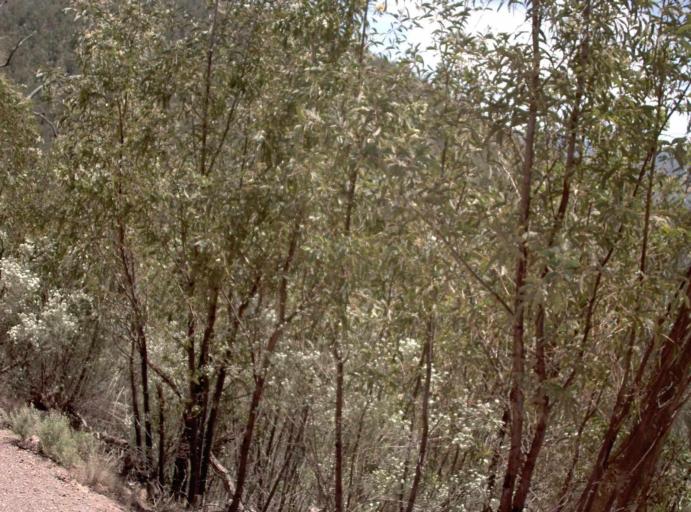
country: AU
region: New South Wales
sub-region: Snowy River
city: Jindabyne
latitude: -37.0056
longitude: 148.2976
